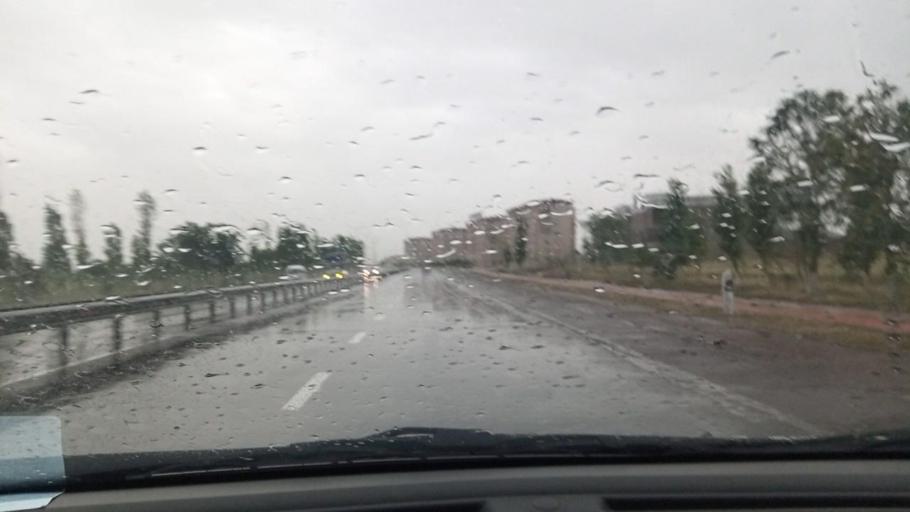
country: UZ
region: Toshkent
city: Ohangaron
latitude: 40.9164
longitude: 69.6057
